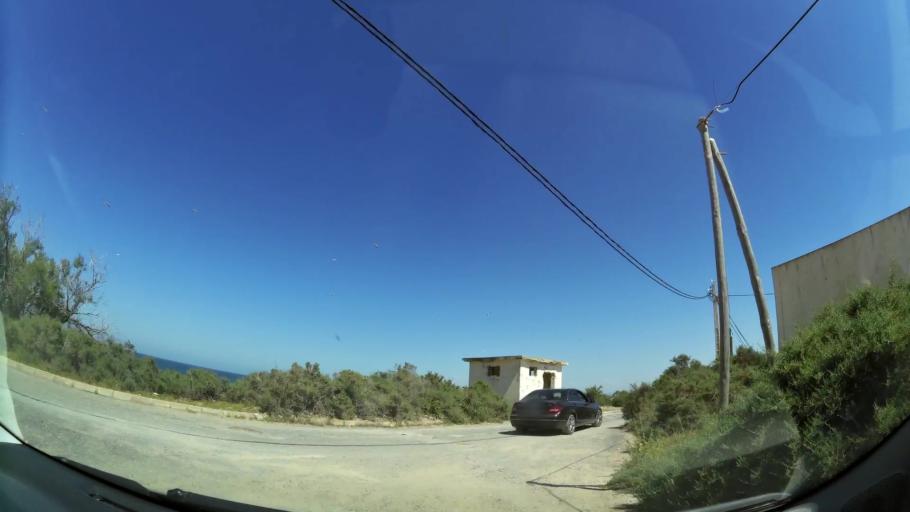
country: MA
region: Oriental
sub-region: Berkane-Taourirt
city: Madagh
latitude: 35.1418
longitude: -2.4261
